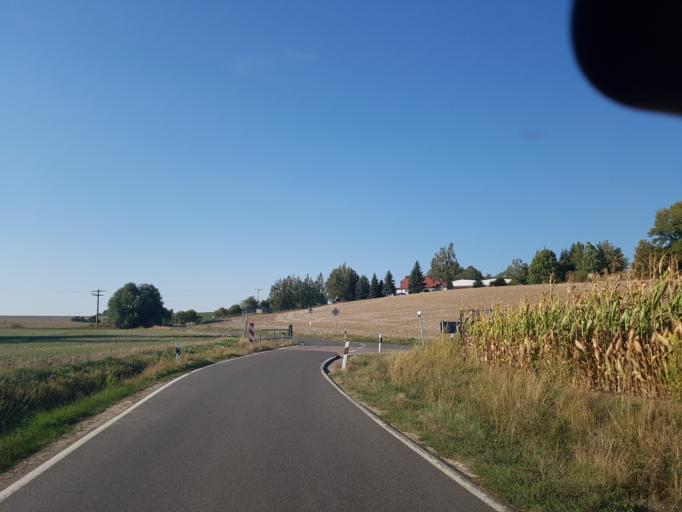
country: DE
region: Saxony
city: Ostrau
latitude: 51.1844
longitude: 13.1122
